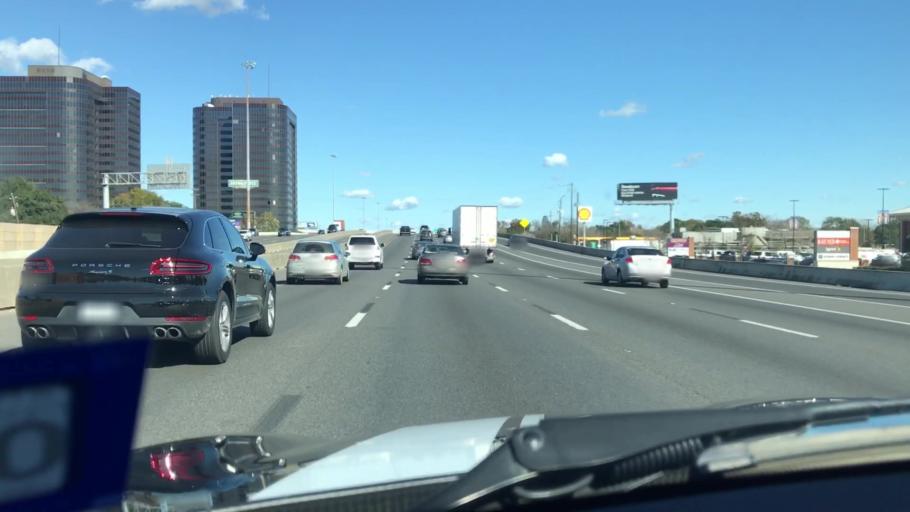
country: US
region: Texas
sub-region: Harris County
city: Bellaire
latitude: 29.6985
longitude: -95.5197
